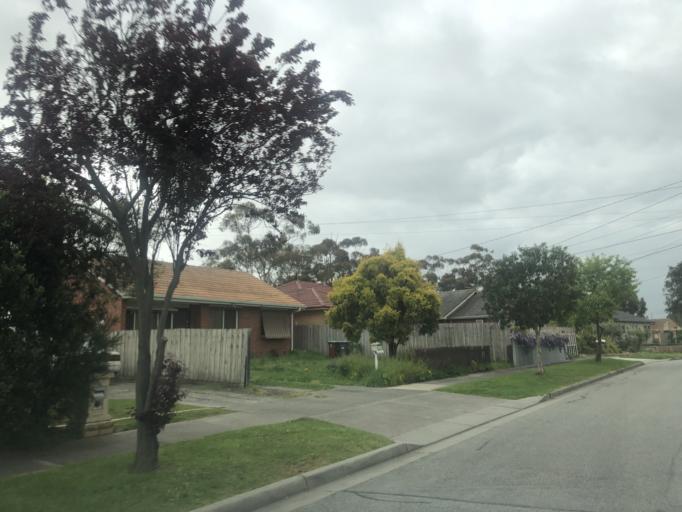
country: AU
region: Victoria
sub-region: Casey
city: Doveton
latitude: -37.9820
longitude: 145.2346
